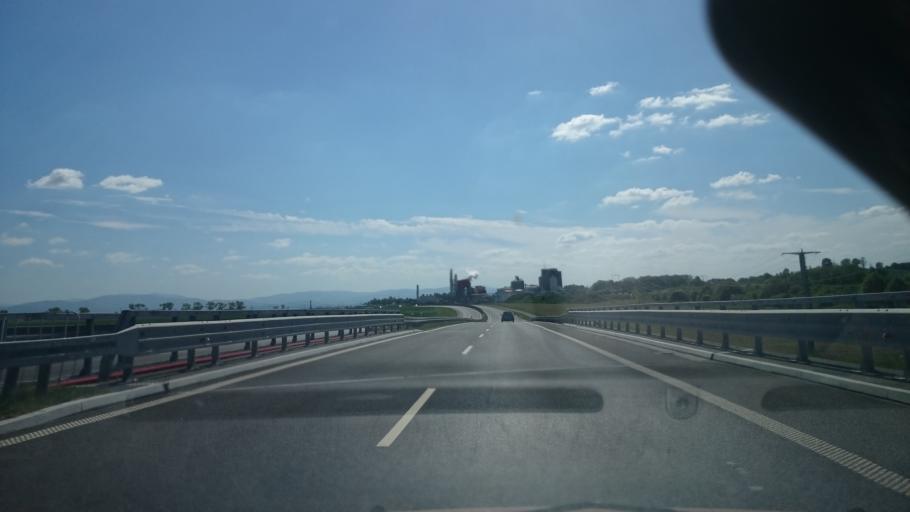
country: PL
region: Opole Voivodeship
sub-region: Powiat nyski
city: Nysa
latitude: 50.4867
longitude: 17.2729
